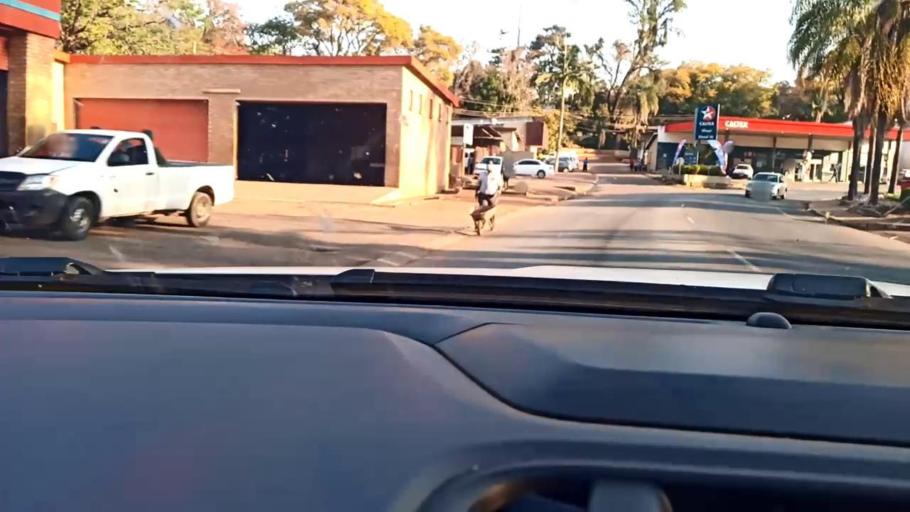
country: ZA
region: Limpopo
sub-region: Mopani District Municipality
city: Duiwelskloof
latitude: -23.6940
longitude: 30.1468
